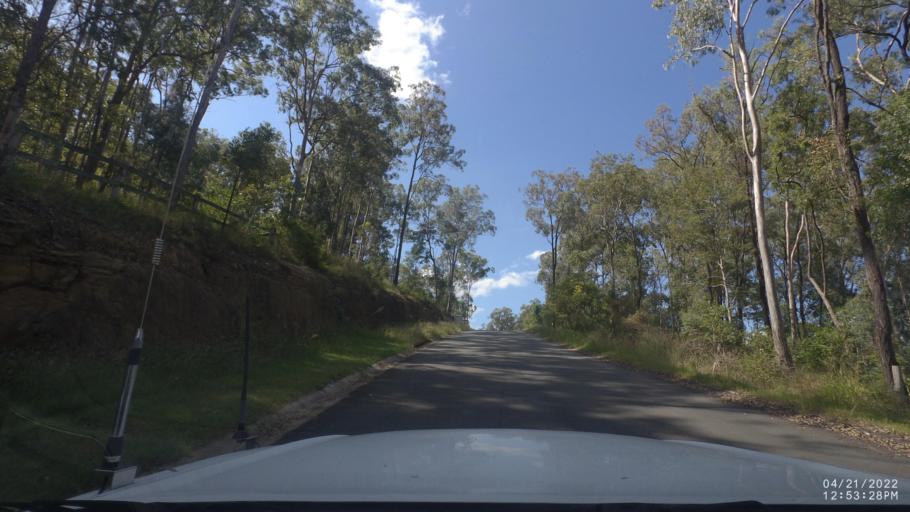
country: AU
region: Queensland
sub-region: Logan
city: Cedar Vale
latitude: -27.8383
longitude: 153.0989
